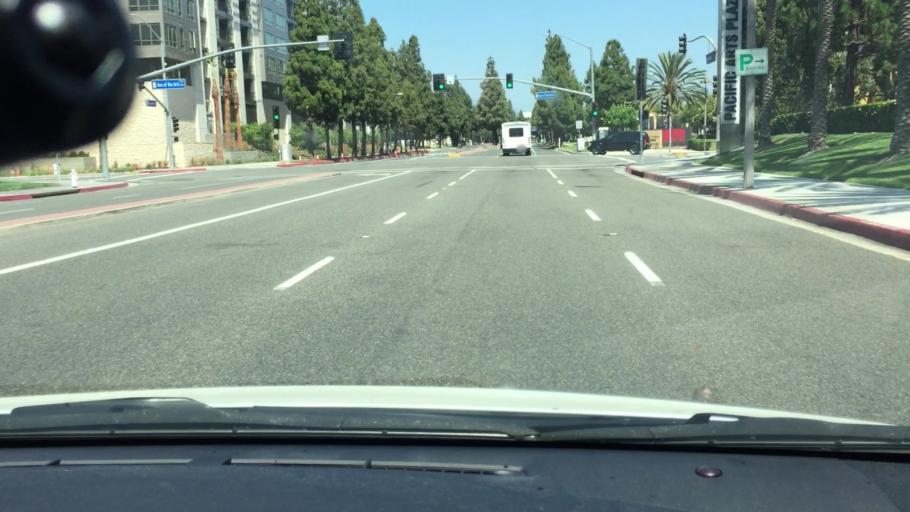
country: US
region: California
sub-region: Orange County
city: Santa Ana
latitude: 33.6901
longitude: -117.8816
